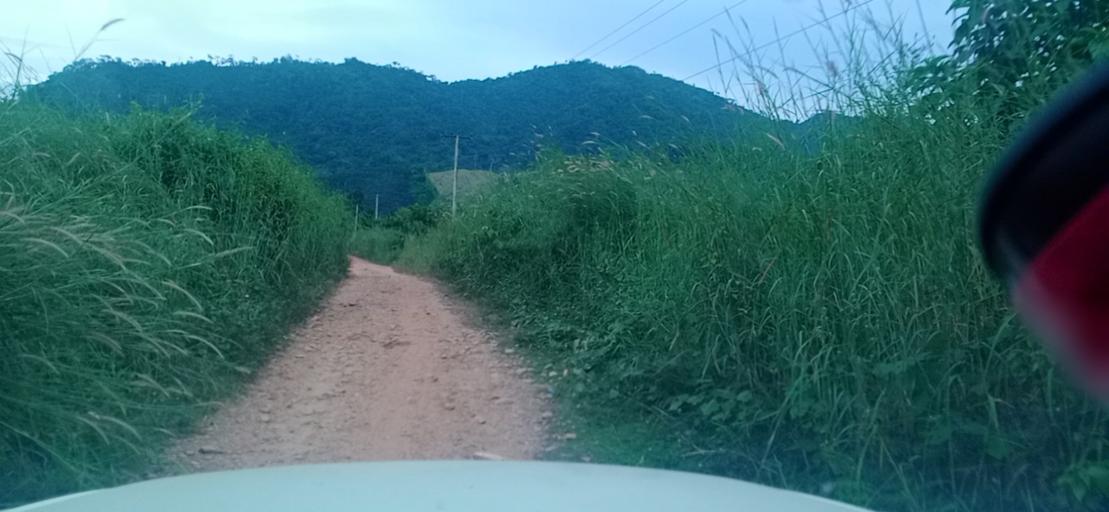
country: TH
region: Changwat Bueng Kan
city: Pak Khat
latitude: 18.5652
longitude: 103.3067
